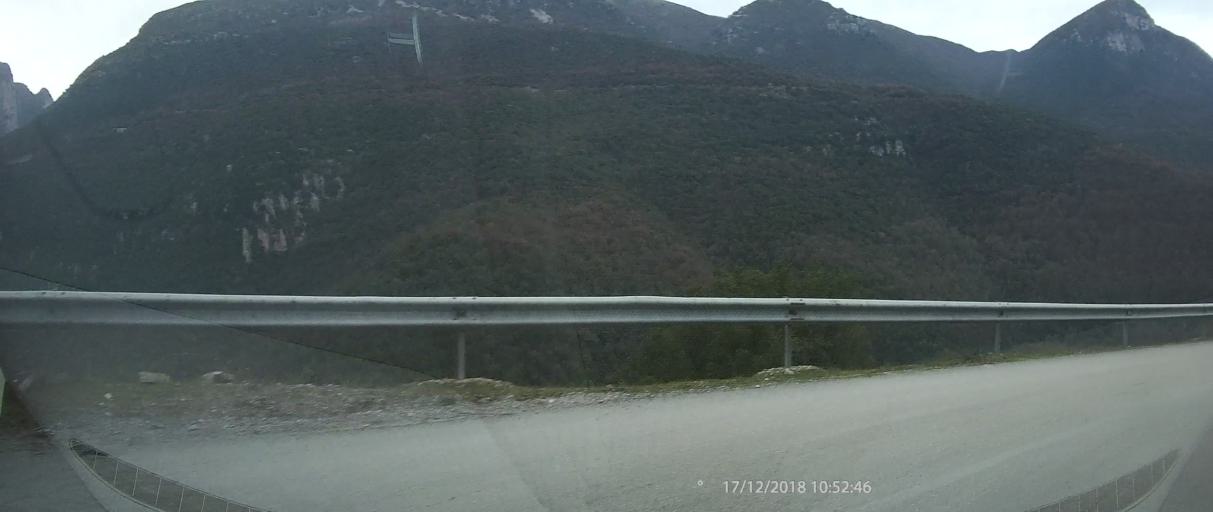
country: GR
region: Epirus
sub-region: Nomos Ioanninon
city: Kalpaki
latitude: 39.9495
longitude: 20.6893
